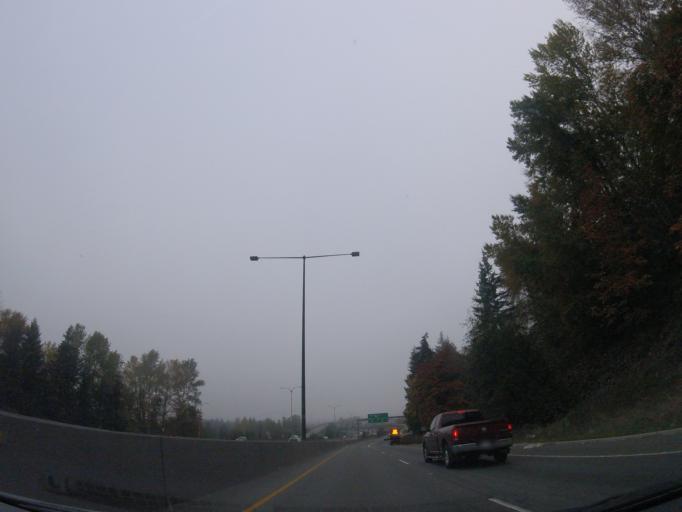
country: US
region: Washington
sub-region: King County
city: Bothell
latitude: 47.7542
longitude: -122.1858
